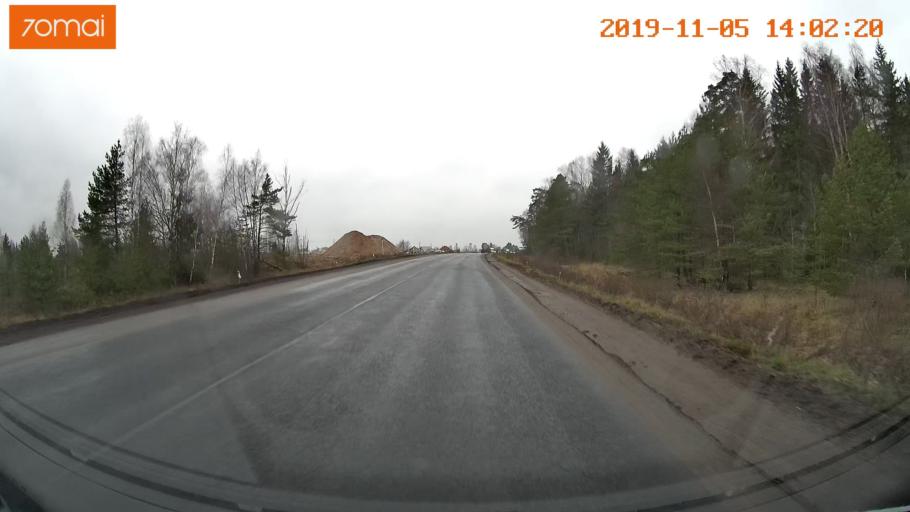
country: RU
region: Ivanovo
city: Kokhma
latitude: 57.0024
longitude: 41.2153
